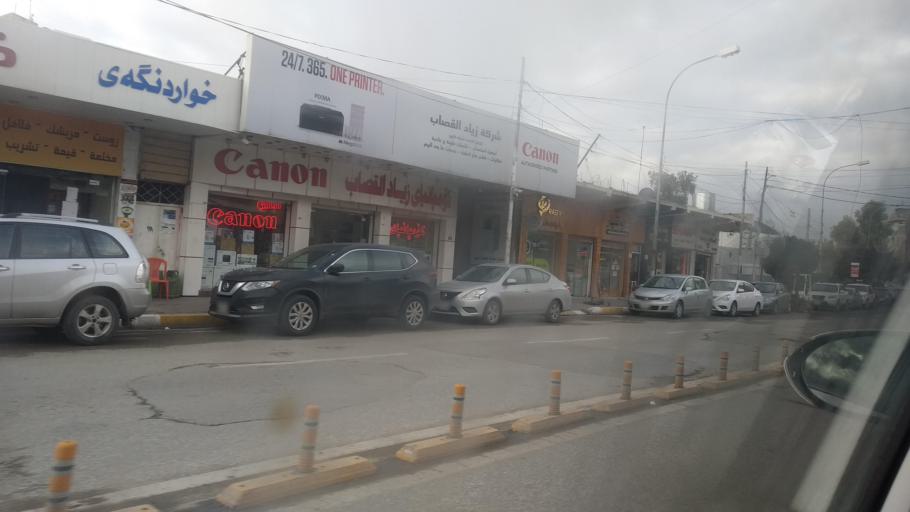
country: IQ
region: Arbil
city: Erbil
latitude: 36.1941
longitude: 44.0132
